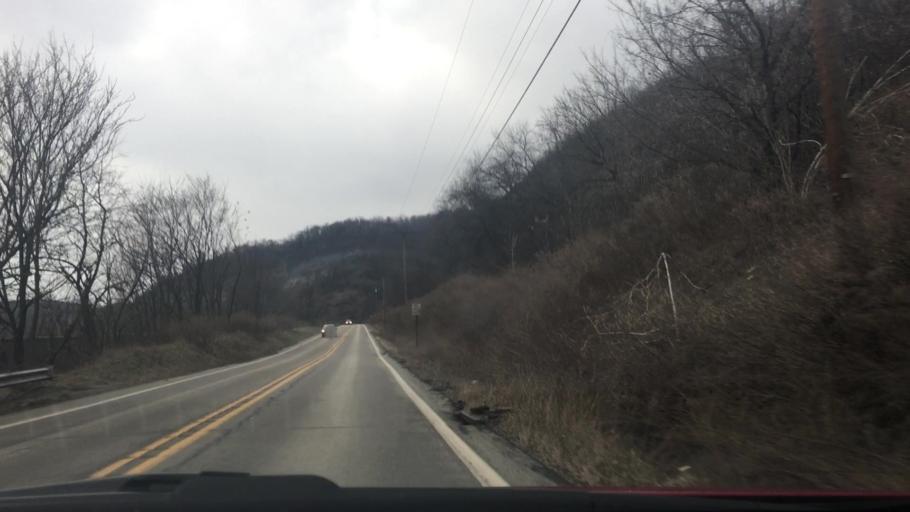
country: US
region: Pennsylvania
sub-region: Allegheny County
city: Clairton
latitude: 40.3083
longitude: -79.8726
